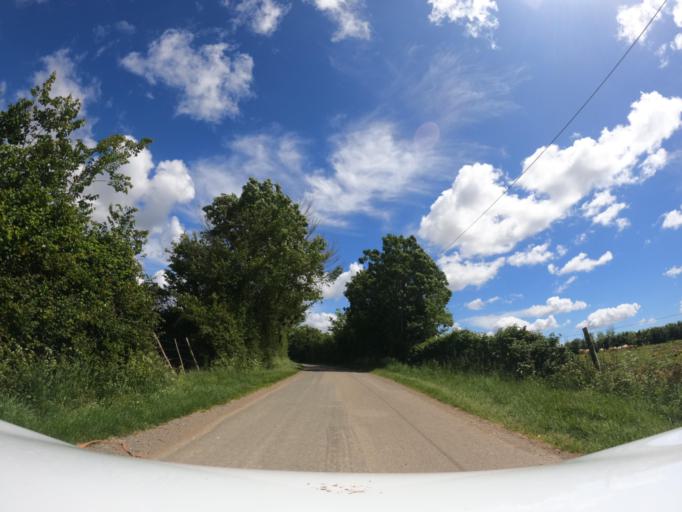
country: FR
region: Pays de la Loire
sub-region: Departement de la Vendee
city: Le Champ-Saint-Pere
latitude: 46.4778
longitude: -1.3179
